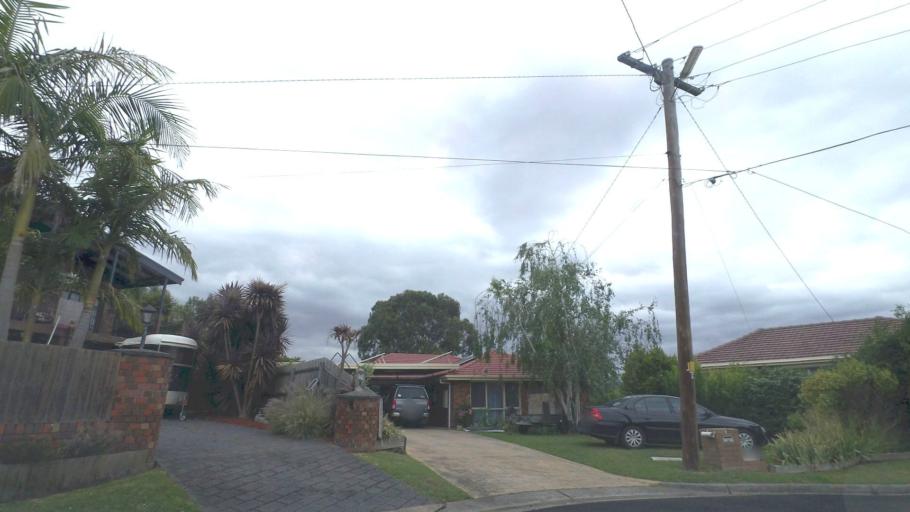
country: AU
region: Victoria
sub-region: Yarra Ranges
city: Lilydale
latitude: -37.7489
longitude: 145.3462
